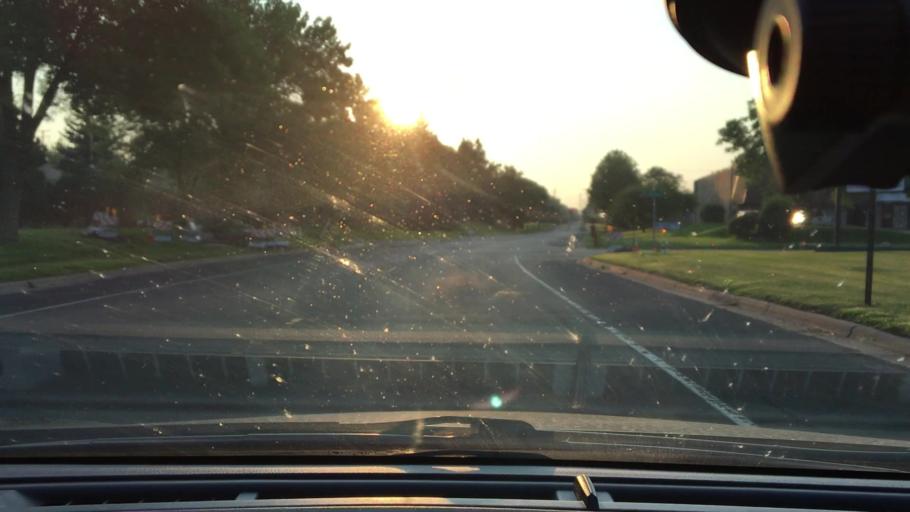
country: US
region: Minnesota
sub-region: Hennepin County
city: Golden Valley
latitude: 44.9890
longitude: -93.3934
